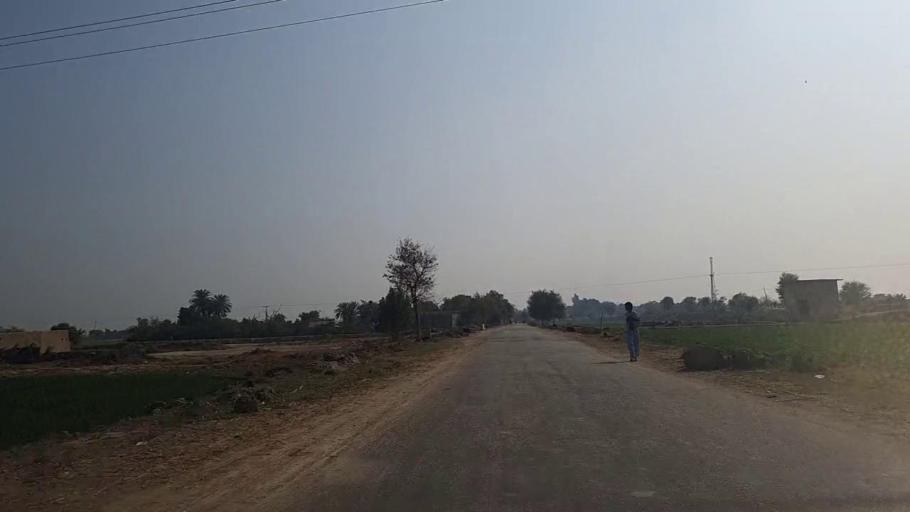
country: PK
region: Sindh
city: Jam Sahib
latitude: 26.3372
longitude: 68.5352
